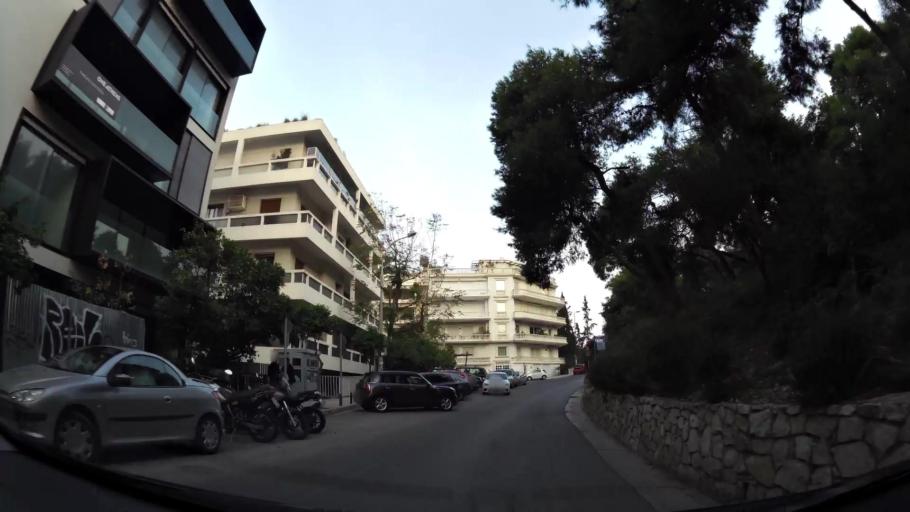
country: GR
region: Attica
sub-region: Nomarchia Athinas
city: Kipseli
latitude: 37.9809
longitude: 23.7406
